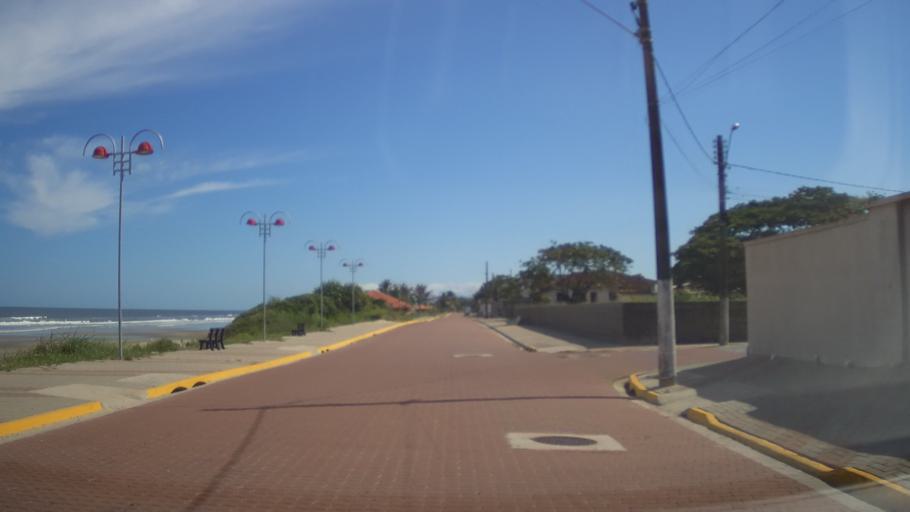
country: BR
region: Sao Paulo
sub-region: Itanhaem
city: Itanhaem
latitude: -24.1689
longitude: -46.7555
